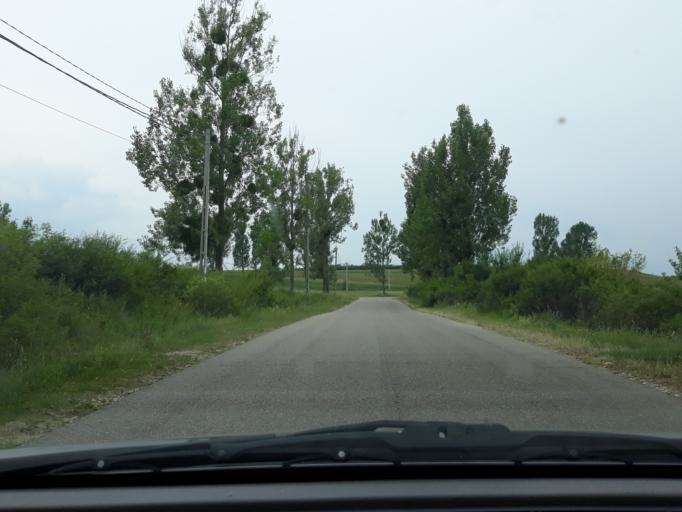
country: RO
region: Salaj
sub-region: Comuna Criseni
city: Criseni
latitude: 47.2459
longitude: 23.0699
